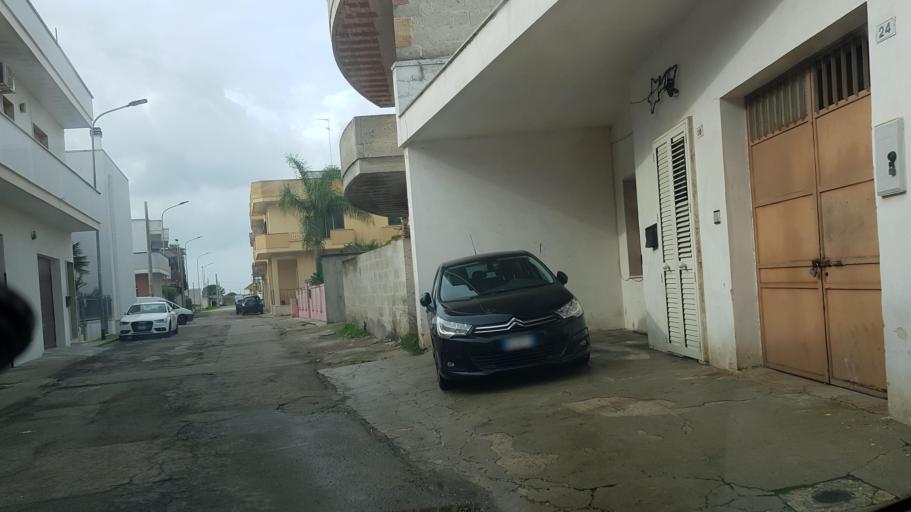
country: IT
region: Apulia
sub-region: Provincia di Lecce
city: Carmiano
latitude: 40.3449
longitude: 18.0359
